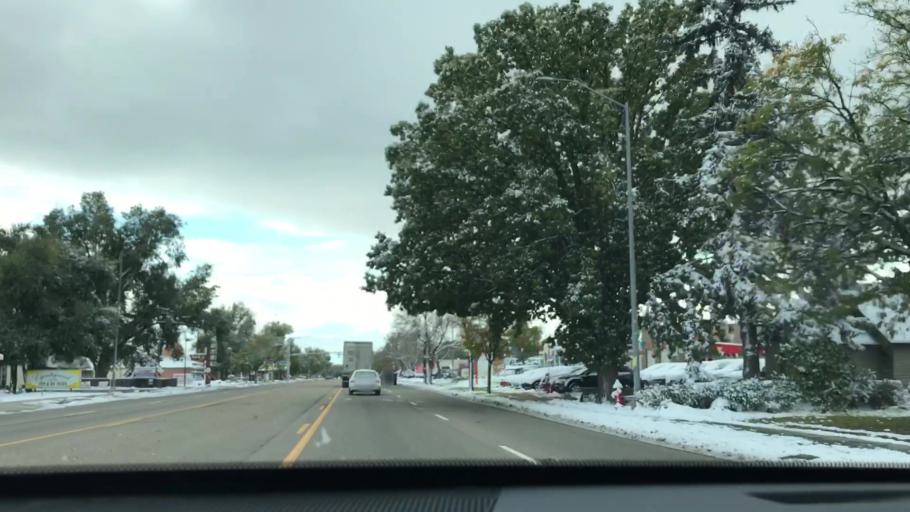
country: US
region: Colorado
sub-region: Boulder County
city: Longmont
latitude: 40.1869
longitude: -105.1024
